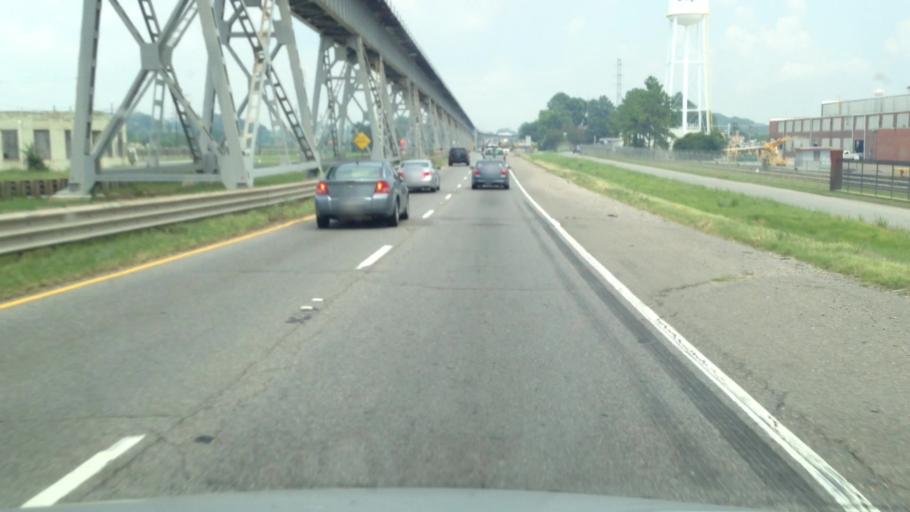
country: US
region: Louisiana
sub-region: West Baton Rouge Parish
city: Port Allen
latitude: 30.5073
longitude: -91.1890
